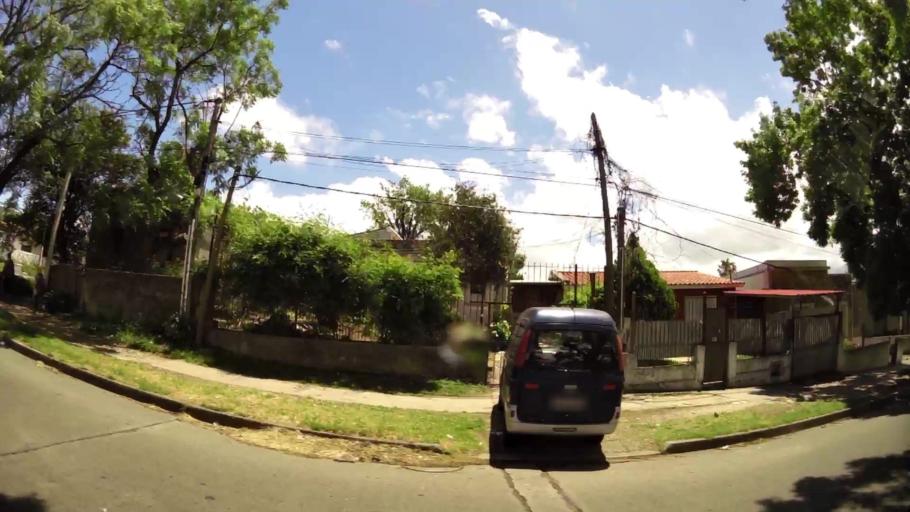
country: UY
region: Montevideo
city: Montevideo
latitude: -34.8520
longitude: -56.1806
